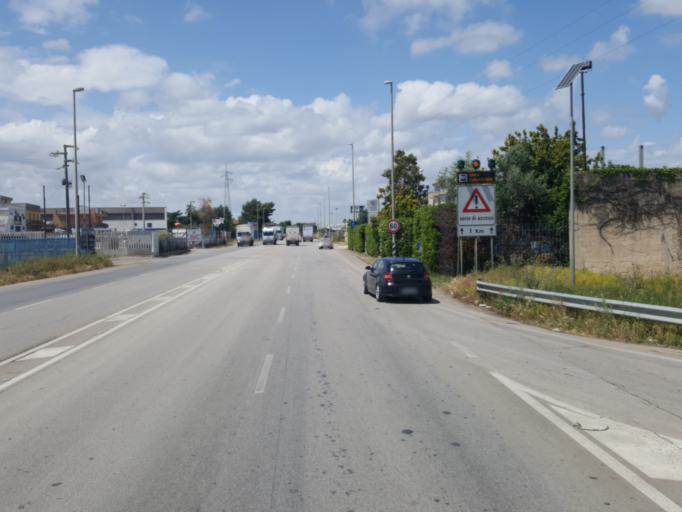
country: IT
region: Apulia
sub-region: Provincia di Bari
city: Modugno
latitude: 41.0920
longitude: 16.7572
